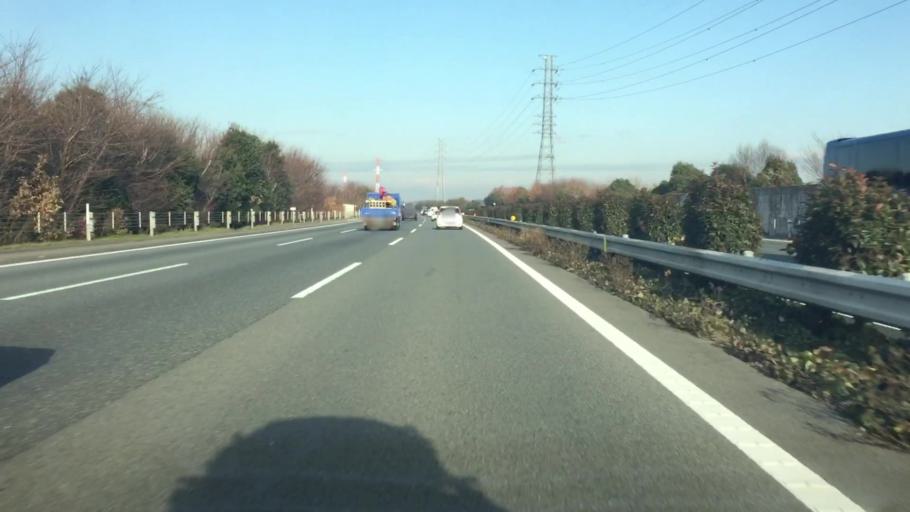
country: JP
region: Saitama
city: Yorii
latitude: 36.1528
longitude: 139.2183
